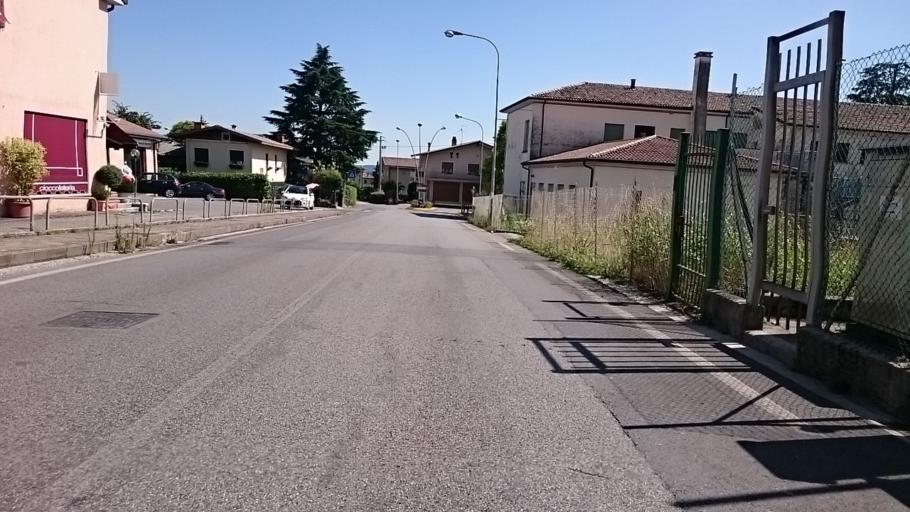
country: IT
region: Veneto
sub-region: Provincia di Treviso
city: Col San Martino
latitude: 45.8950
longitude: 12.0853
